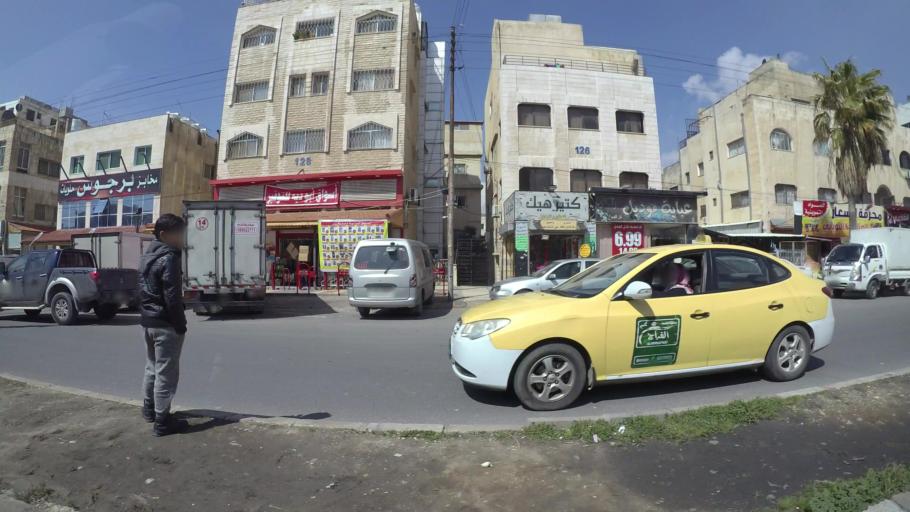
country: JO
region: Amman
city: Al Quwaysimah
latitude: 31.9309
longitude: 35.9109
